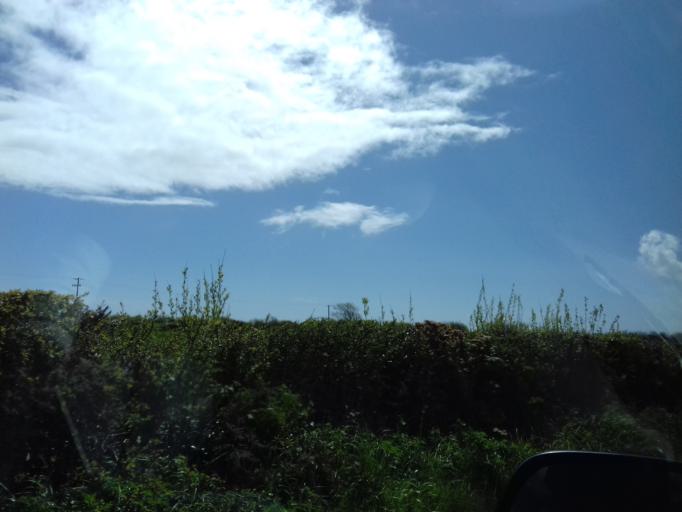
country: IE
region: Munster
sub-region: Waterford
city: Dunmore East
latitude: 52.2305
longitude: -6.8623
